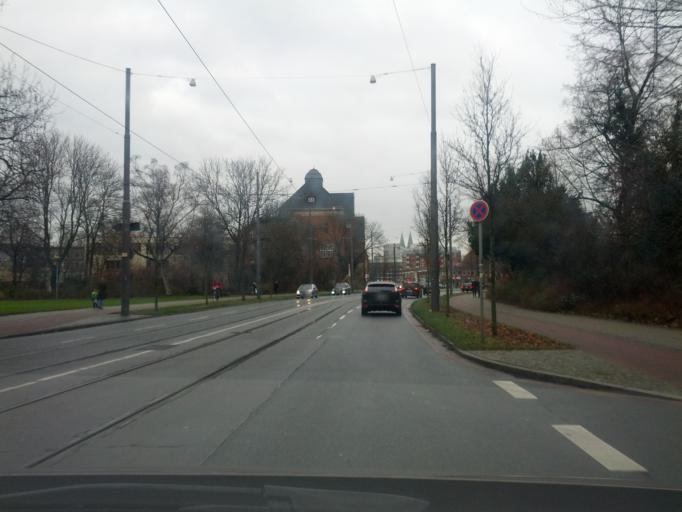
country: DE
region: Bremen
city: Bremen
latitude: 53.0686
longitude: 8.7970
